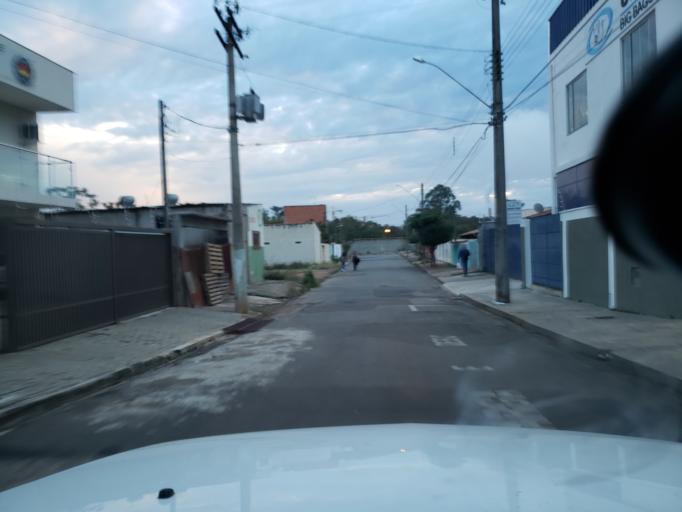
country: BR
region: Sao Paulo
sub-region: Moji-Guacu
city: Mogi-Gaucu
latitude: -22.3649
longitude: -46.9511
